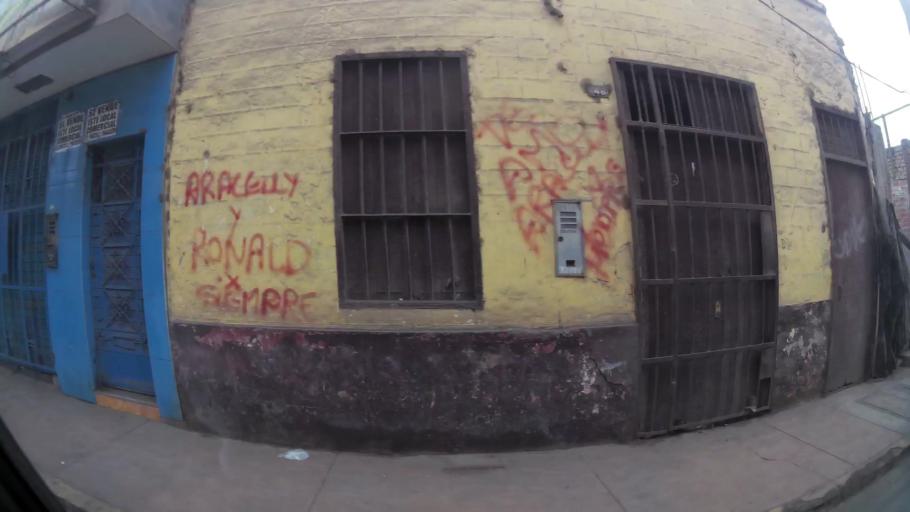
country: PE
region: Lima
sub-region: Provincia de Huaral
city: Huaral
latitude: -11.4971
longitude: -77.2084
